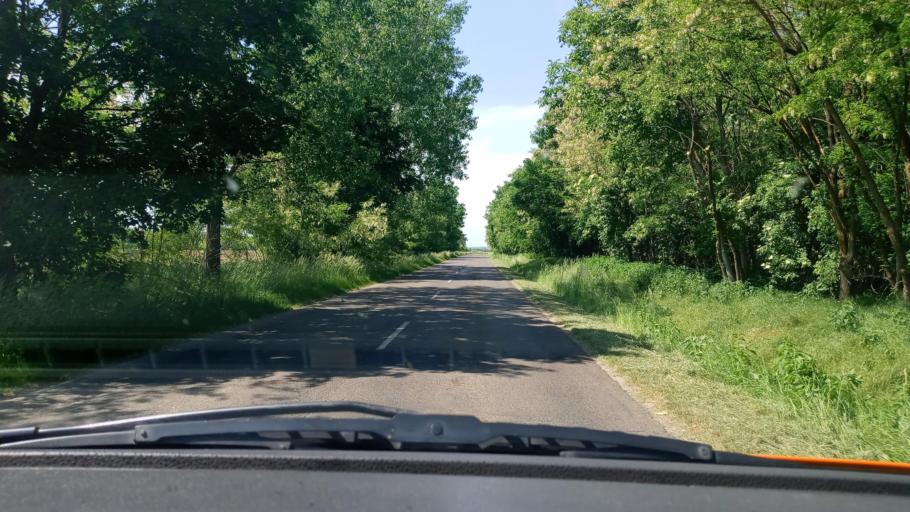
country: HU
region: Baranya
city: Harkany
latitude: 45.8970
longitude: 18.1678
